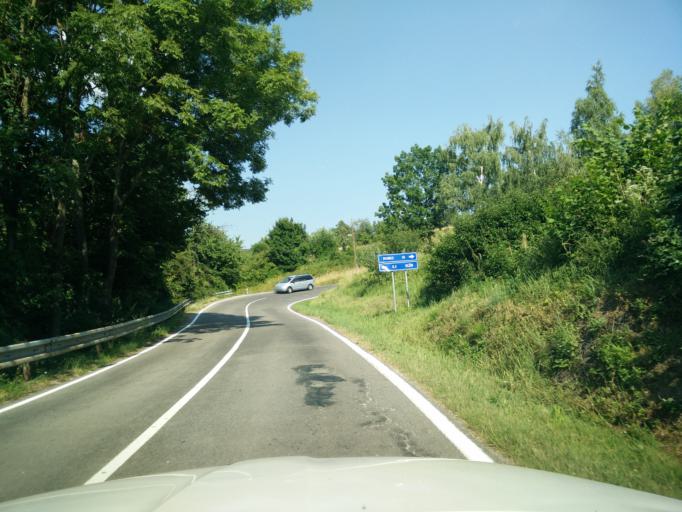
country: SK
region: Nitriansky
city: Bojnice
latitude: 48.8082
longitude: 18.5117
